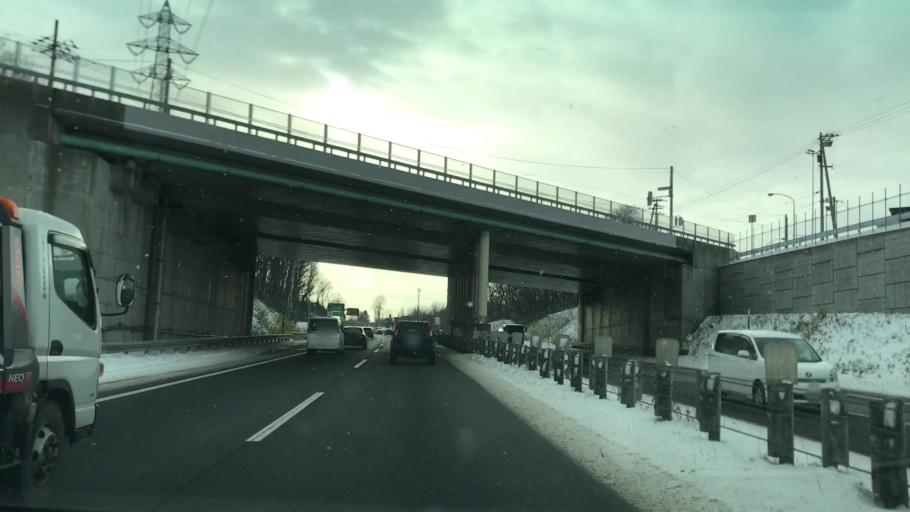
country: JP
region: Hokkaido
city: Kitahiroshima
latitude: 42.9843
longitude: 141.4722
